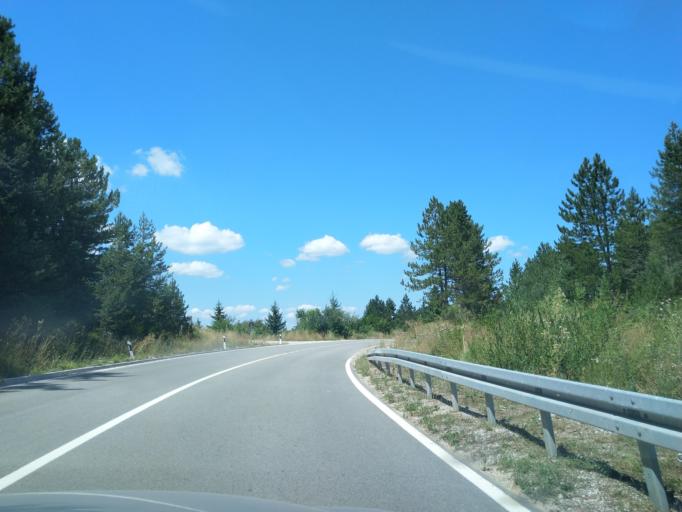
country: RS
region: Central Serbia
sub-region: Zlatiborski Okrug
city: Sjenica
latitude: 43.3095
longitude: 19.8981
